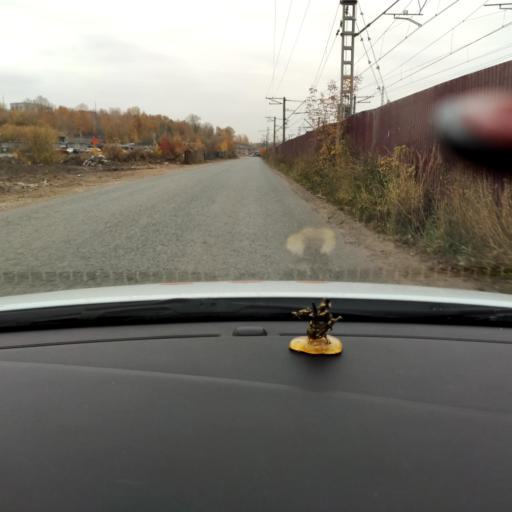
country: RU
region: Tatarstan
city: Verkhniy Uslon
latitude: 55.8038
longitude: 49.0354
